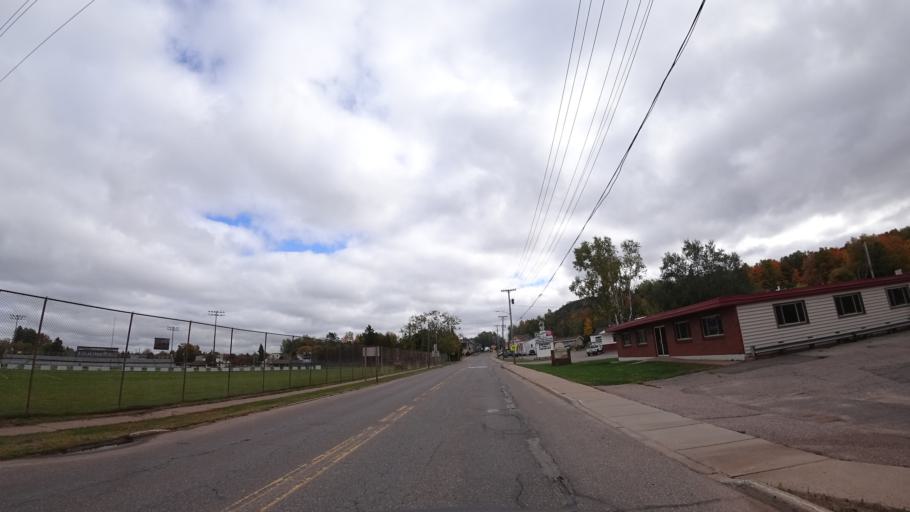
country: US
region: Michigan
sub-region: Marquette County
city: Negaunee
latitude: 46.5059
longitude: -87.6122
